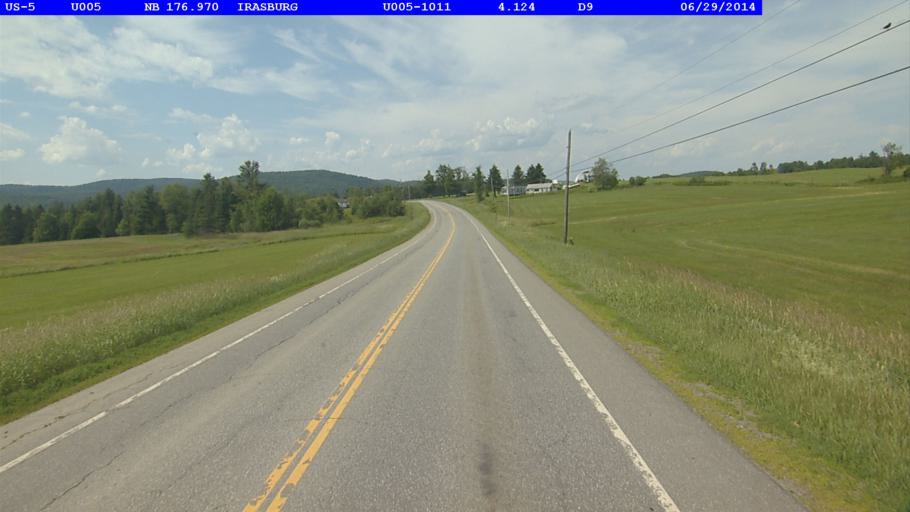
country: US
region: Vermont
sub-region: Orleans County
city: Newport
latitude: 44.8511
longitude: -72.2632
